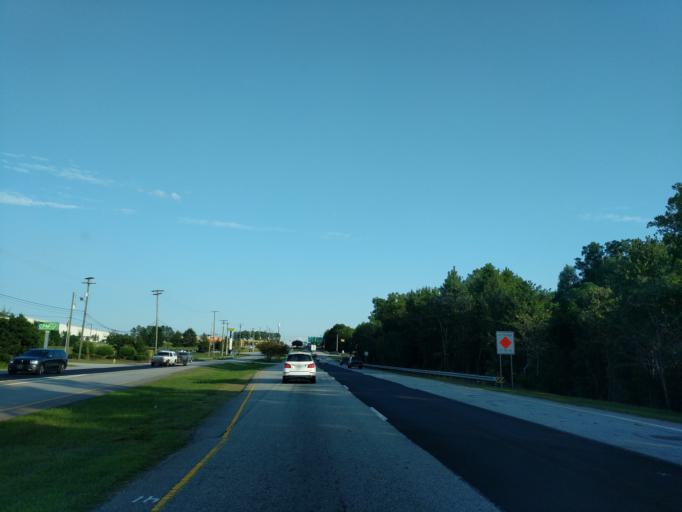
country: US
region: South Carolina
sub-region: Spartanburg County
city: Duncan
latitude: 34.8992
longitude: -82.1674
